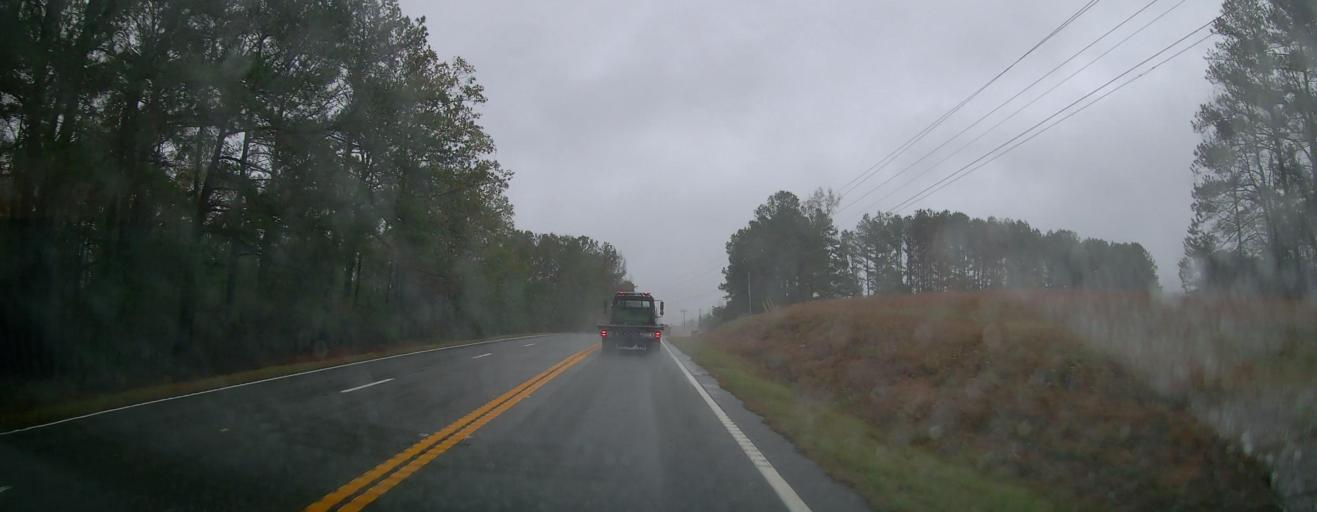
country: US
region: Georgia
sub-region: Jones County
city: Gray
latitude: 33.0508
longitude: -83.5065
